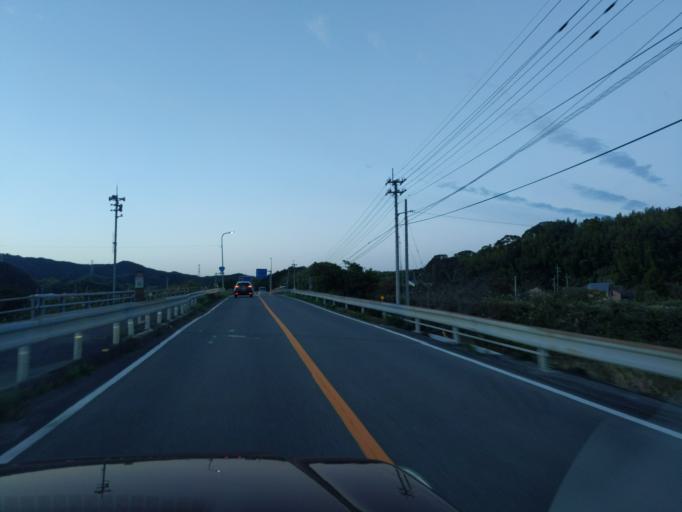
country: JP
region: Tokushima
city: Anan
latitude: 33.8448
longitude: 134.6251
